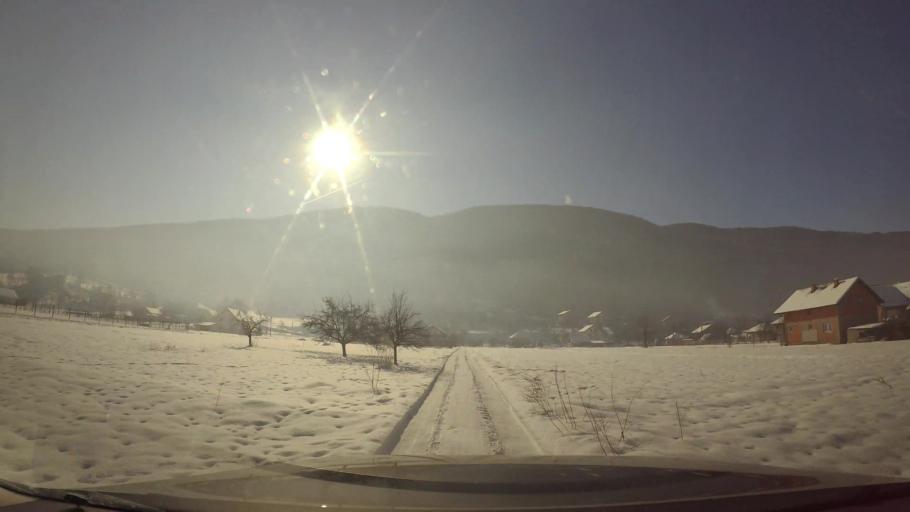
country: BA
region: Federation of Bosnia and Herzegovina
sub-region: Kanton Sarajevo
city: Sarajevo
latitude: 43.7901
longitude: 18.3410
